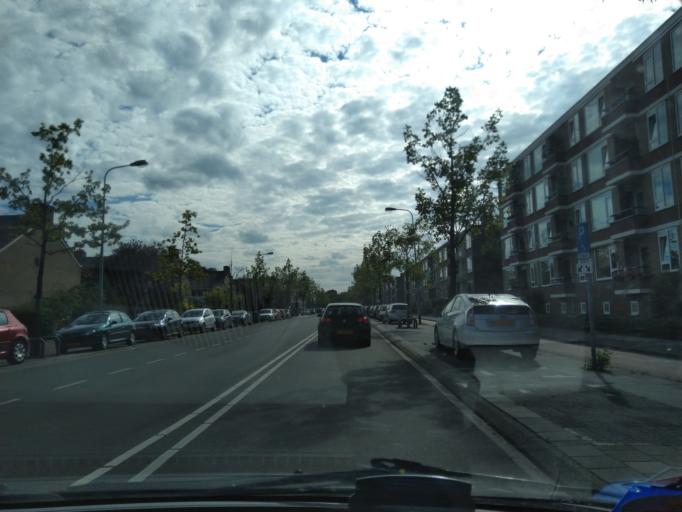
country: NL
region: Groningen
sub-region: Gemeente Groningen
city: Groningen
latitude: 53.1978
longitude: 6.5576
